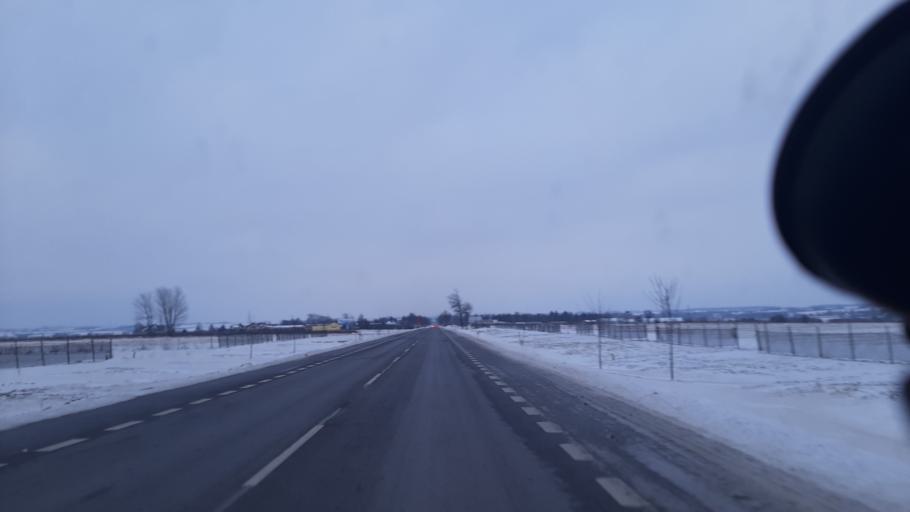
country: PL
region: Lublin Voivodeship
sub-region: Powiat pulawski
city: Markuszow
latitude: 51.3799
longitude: 22.2373
